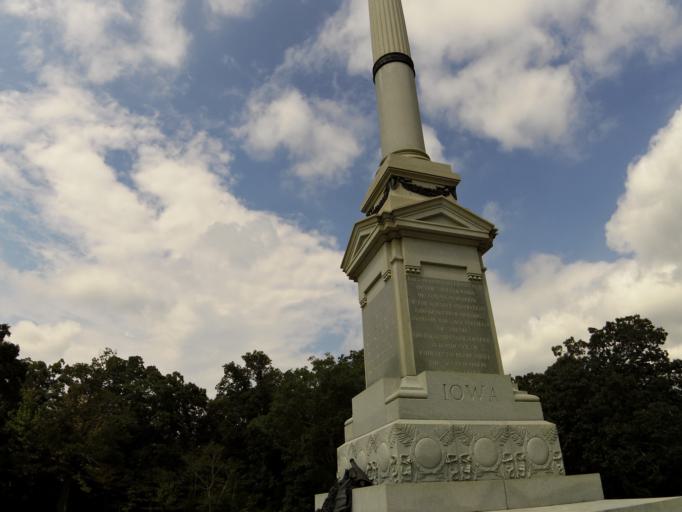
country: US
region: Tennessee
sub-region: Hardin County
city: Crump
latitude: 35.1507
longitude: -88.3244
